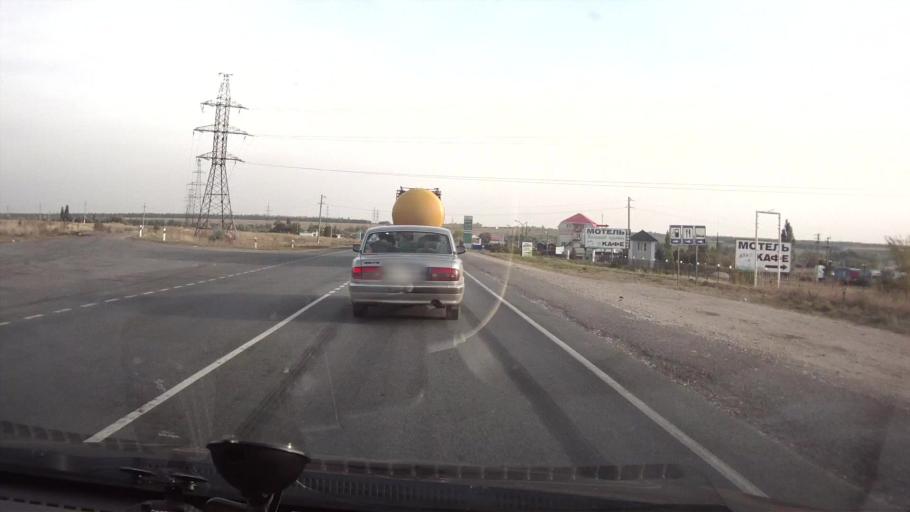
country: RU
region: Saratov
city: Sokolovyy
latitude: 51.5069
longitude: 45.8111
